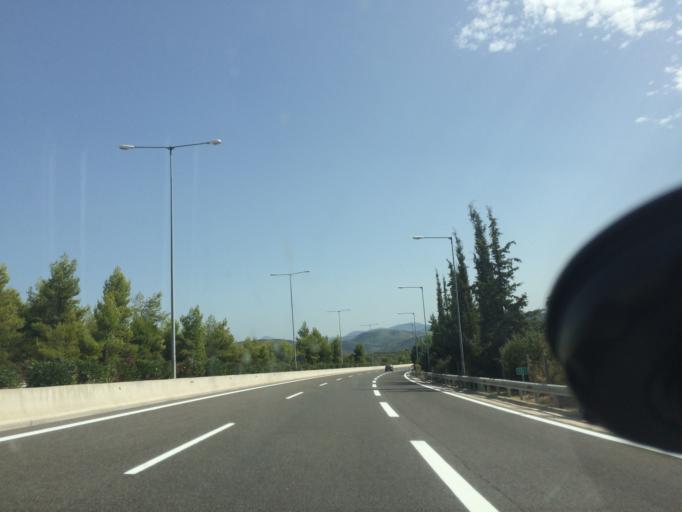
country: GR
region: Central Greece
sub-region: Nomos Fthiotidos
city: Martinon
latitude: 38.5948
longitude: 23.1950
